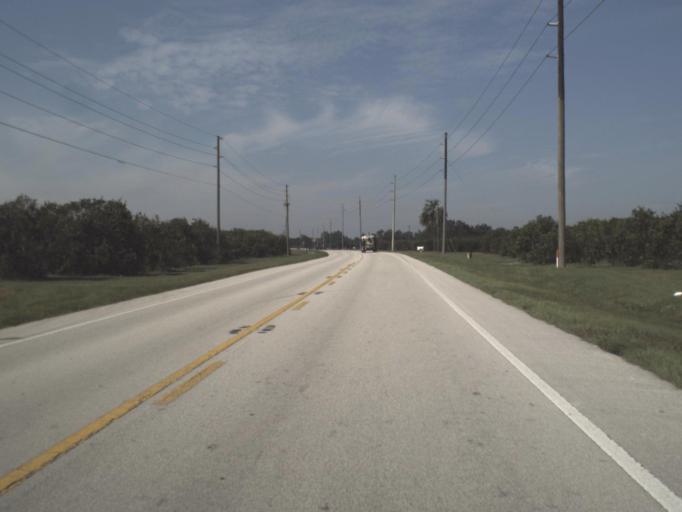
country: US
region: Florida
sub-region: Hardee County
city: Wauchula
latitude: 27.5590
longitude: -81.6740
